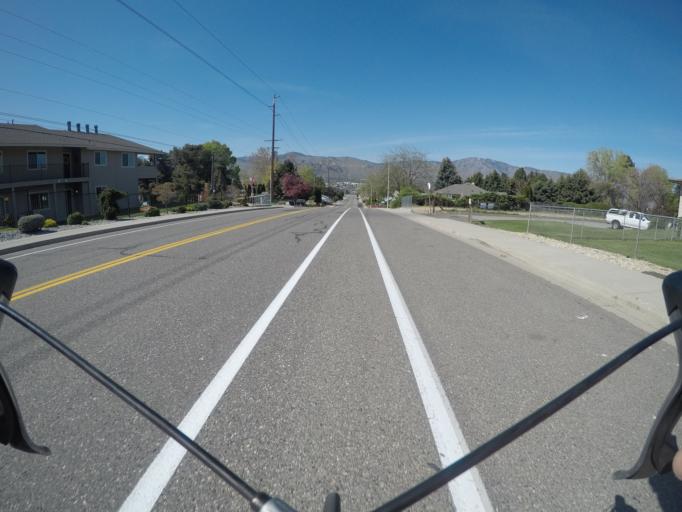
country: US
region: Washington
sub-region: Douglas County
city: East Wenatchee Bench
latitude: 47.4225
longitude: -120.2837
